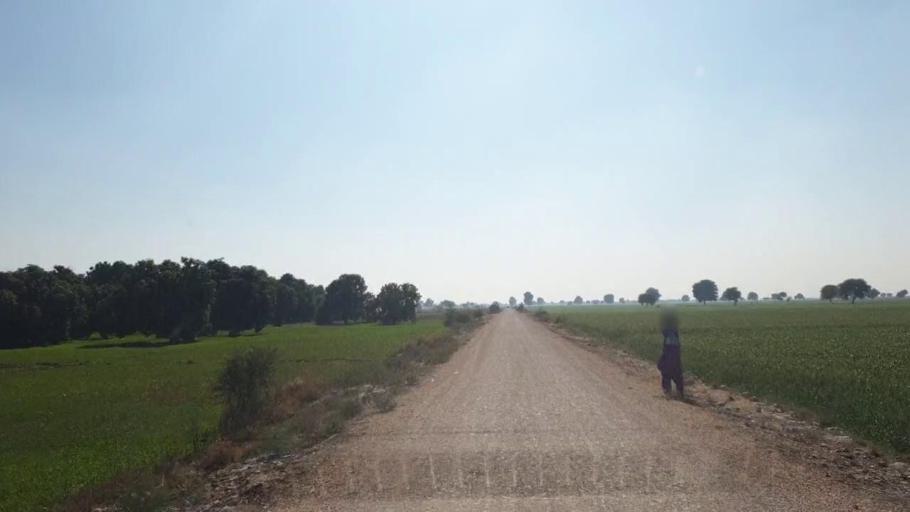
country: PK
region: Sindh
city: Shahpur Chakar
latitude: 26.1076
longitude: 68.6308
